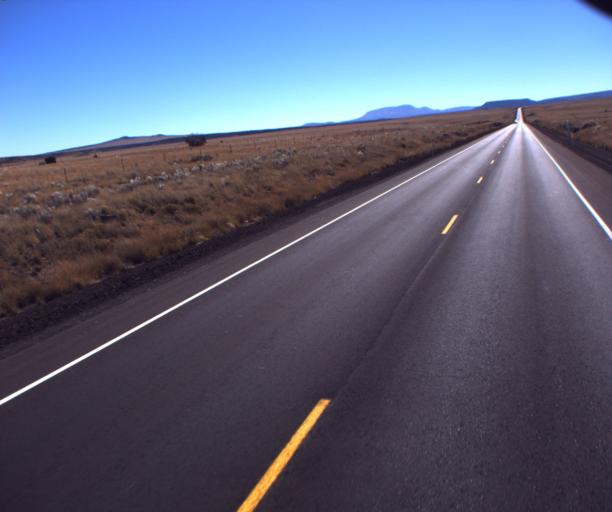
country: US
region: Arizona
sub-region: Apache County
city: Springerville
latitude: 34.2207
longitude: -109.3357
